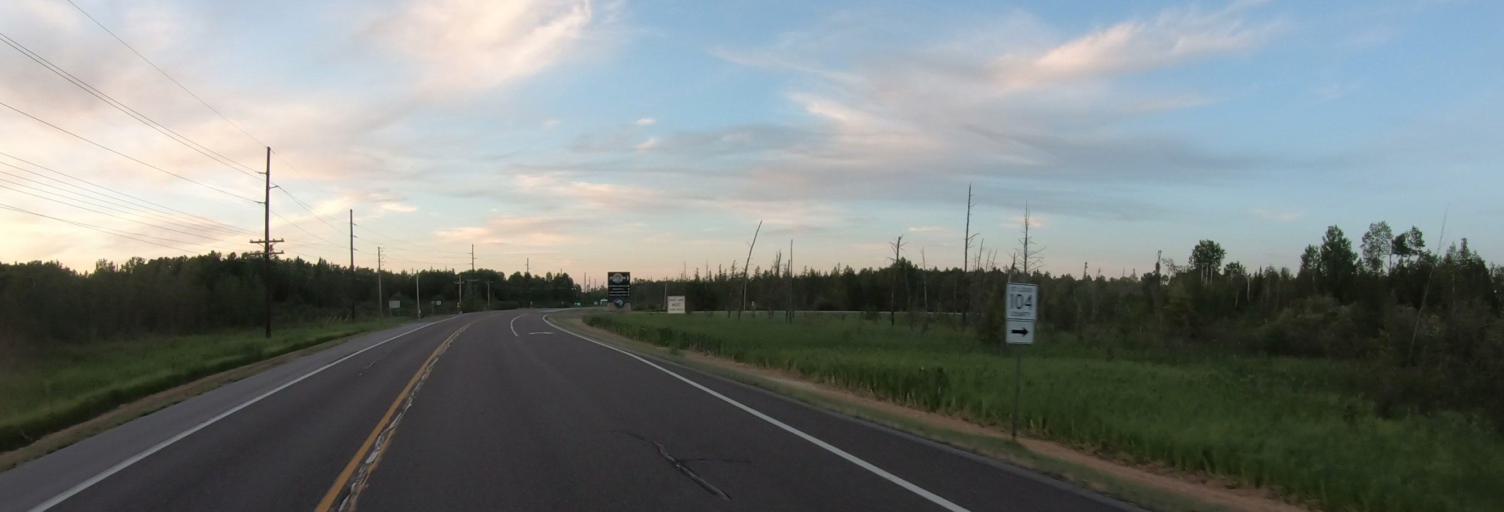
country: US
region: Minnesota
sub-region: Saint Louis County
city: Aurora
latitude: 47.8081
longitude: -92.3726
